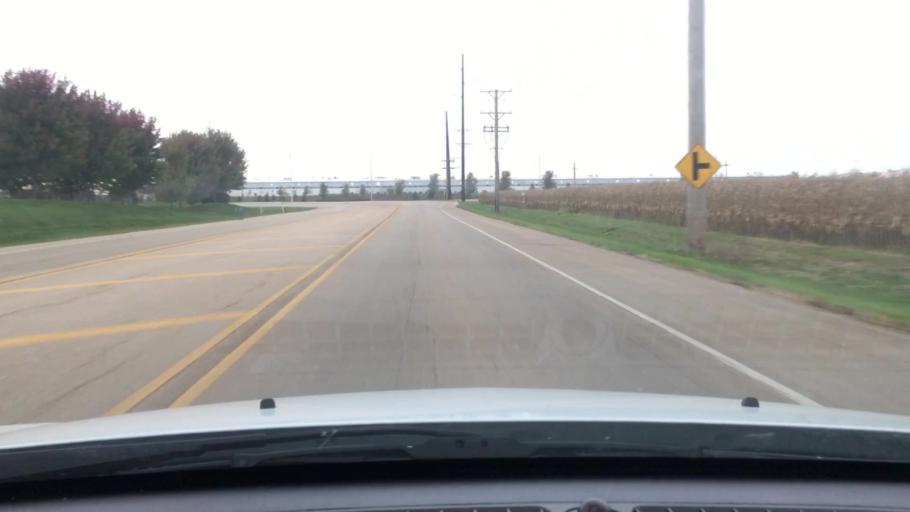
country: US
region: Illinois
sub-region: Ogle County
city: Rochelle
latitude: 41.8959
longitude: -89.0290
